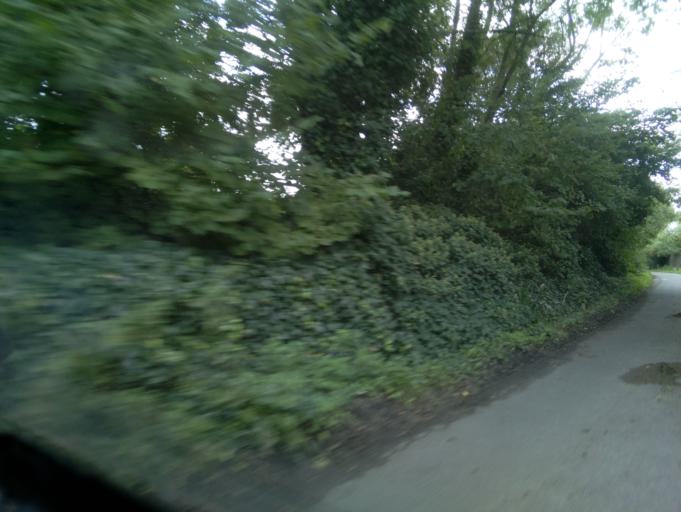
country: GB
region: England
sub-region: Wiltshire
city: Nettleton
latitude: 51.5030
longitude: -2.2648
